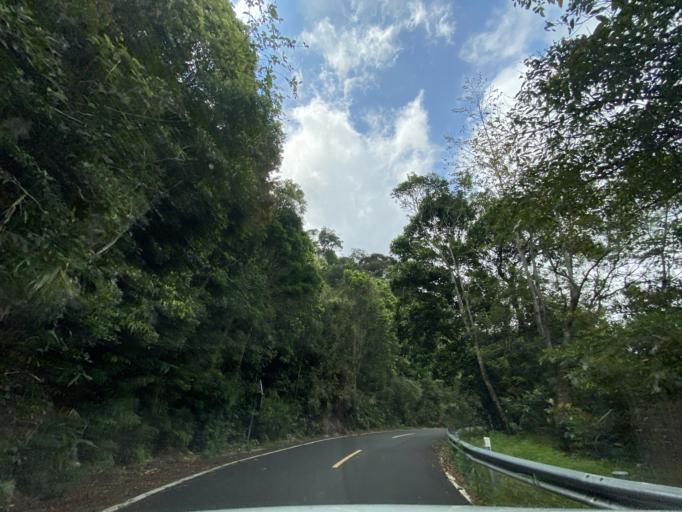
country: CN
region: Hainan
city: Diaoluoshan
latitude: 18.7031
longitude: 109.8826
